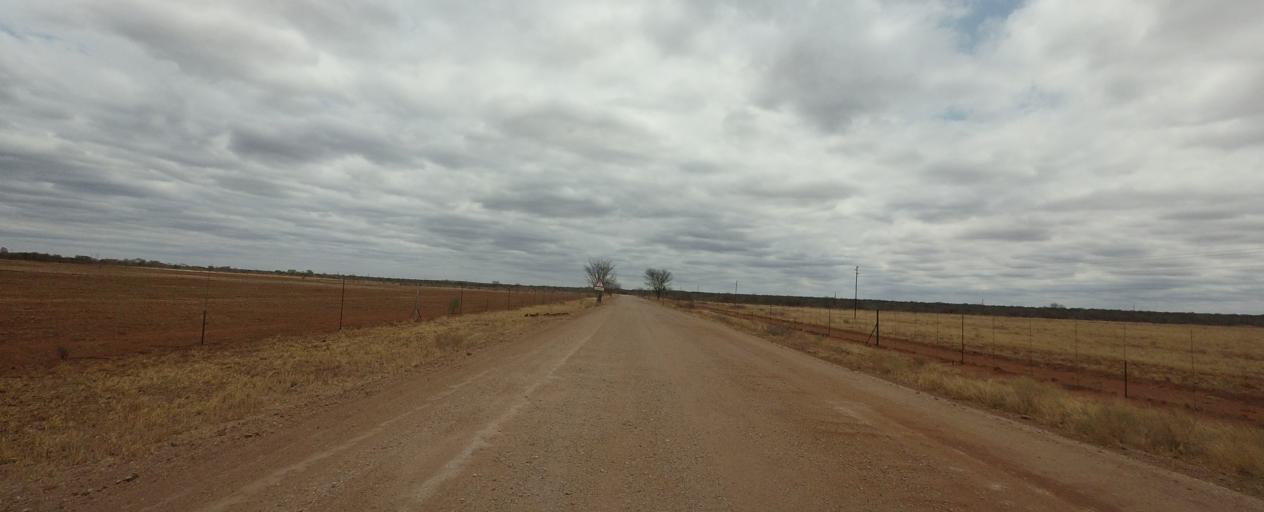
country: BW
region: Central
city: Mathathane
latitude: -22.7105
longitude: 28.5699
